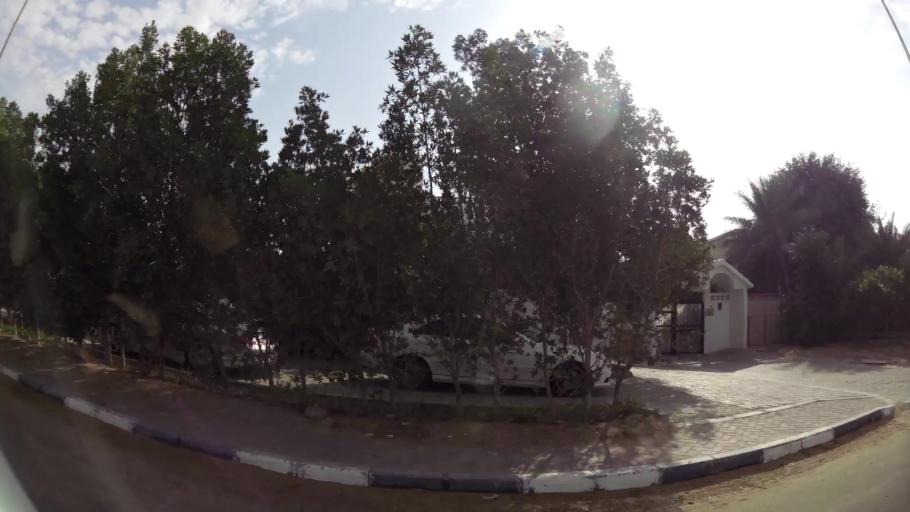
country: AE
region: Abu Dhabi
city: Abu Dhabi
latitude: 24.2532
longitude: 54.7251
